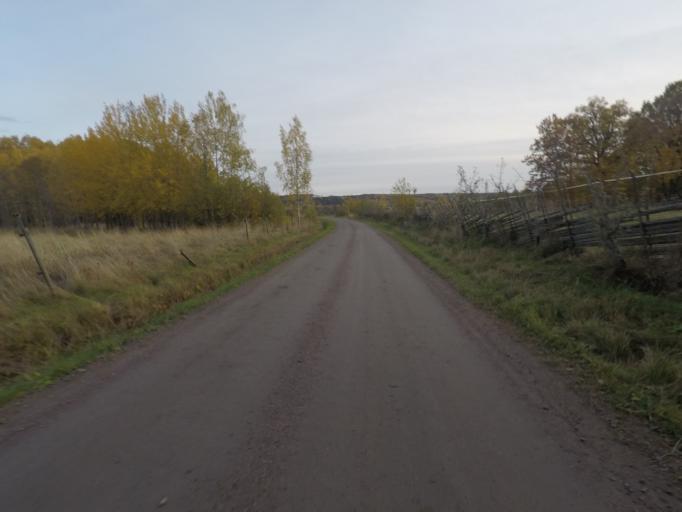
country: SE
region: OErebro
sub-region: Karlskoga Kommun
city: Karlskoga
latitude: 59.2951
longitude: 14.4956
